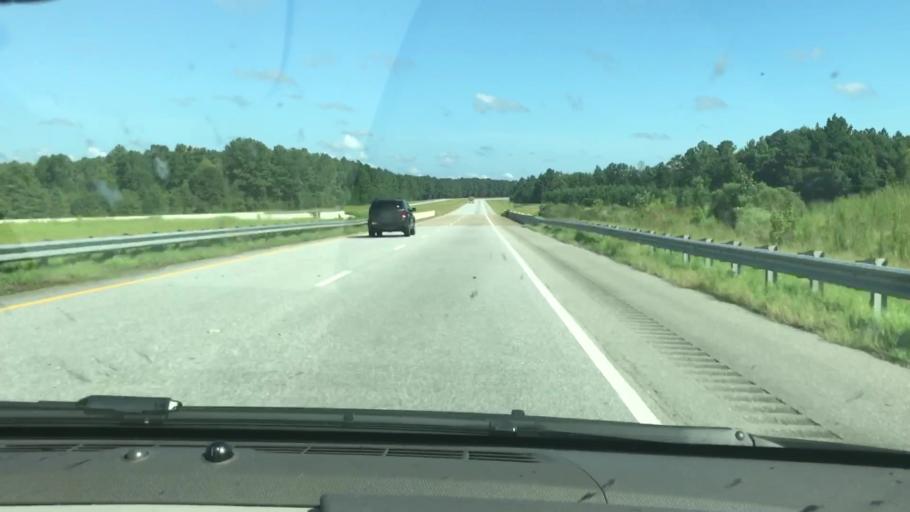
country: US
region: Alabama
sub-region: Barbour County
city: Eufaula
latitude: 32.1808
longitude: -85.1790
